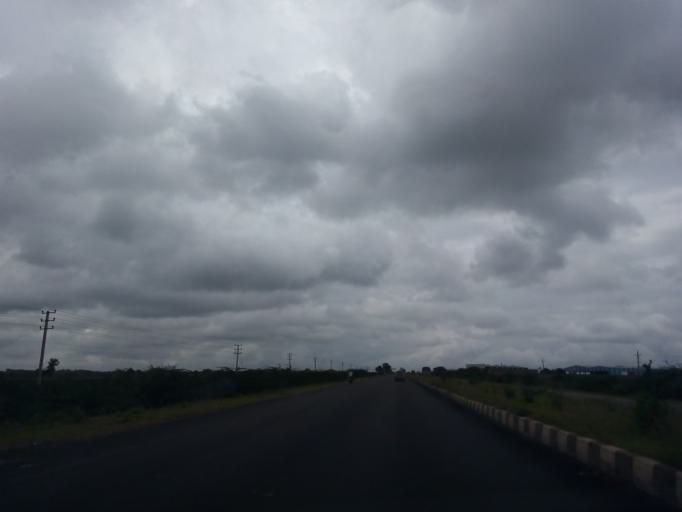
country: IN
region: Karnataka
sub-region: Haveri
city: Ranibennur
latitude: 14.6311
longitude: 75.5888
